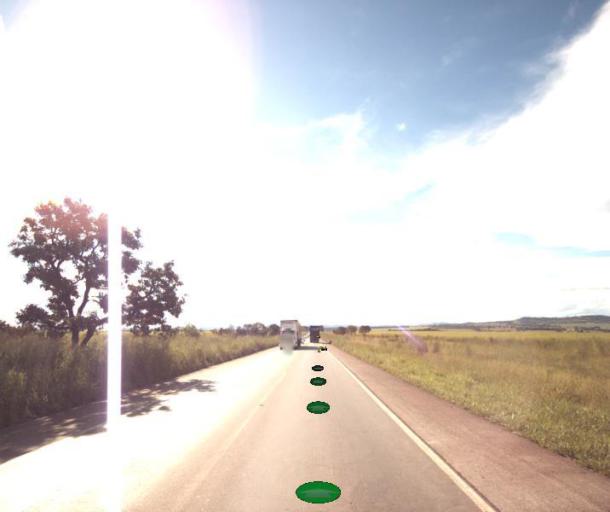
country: BR
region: Goias
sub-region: Rialma
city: Rialma
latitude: -15.4191
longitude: -49.5203
